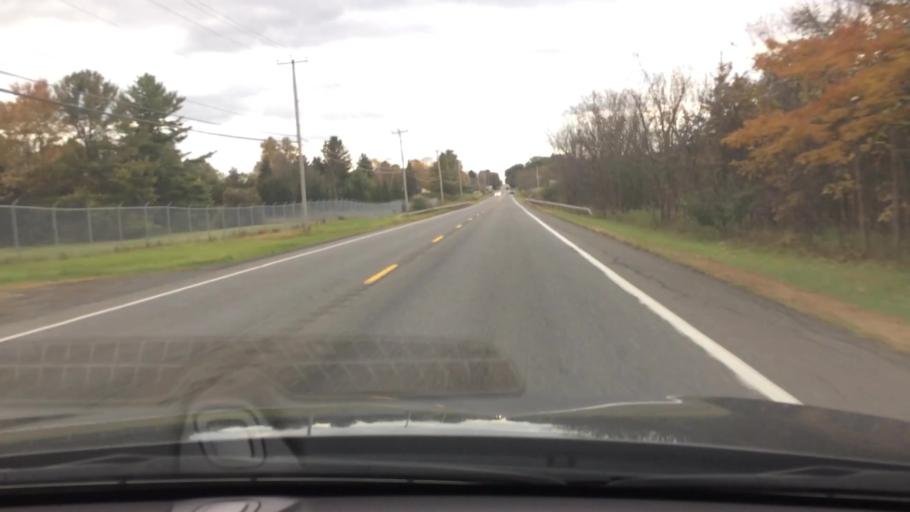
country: US
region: New York
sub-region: Columbia County
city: Stottville
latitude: 42.2914
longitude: -73.7154
